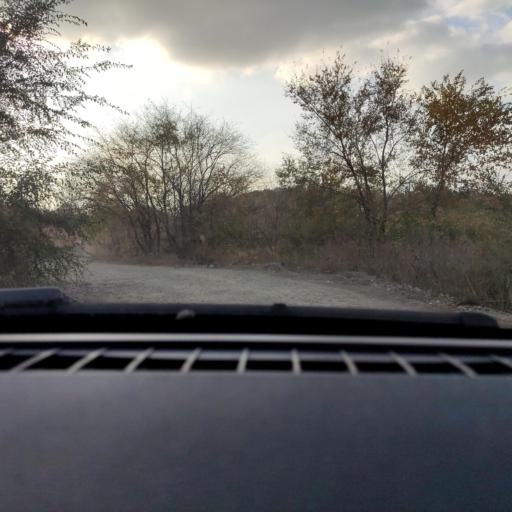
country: RU
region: Voronezj
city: Voronezh
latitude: 51.6685
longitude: 39.2757
